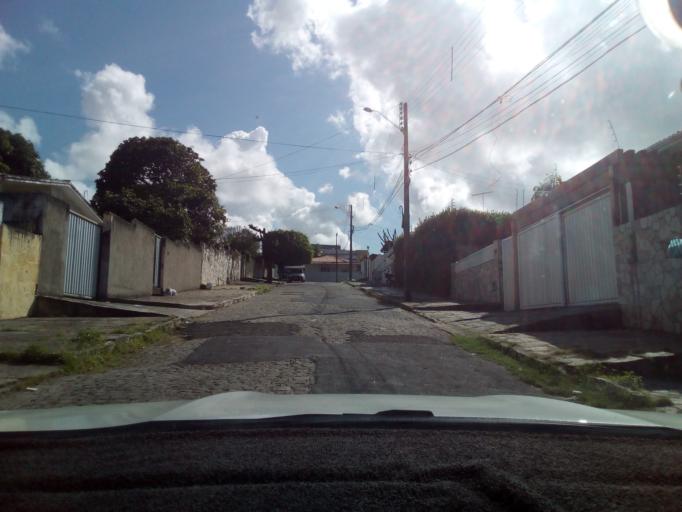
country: BR
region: Paraiba
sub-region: Joao Pessoa
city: Joao Pessoa
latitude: -7.1010
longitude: -34.8545
